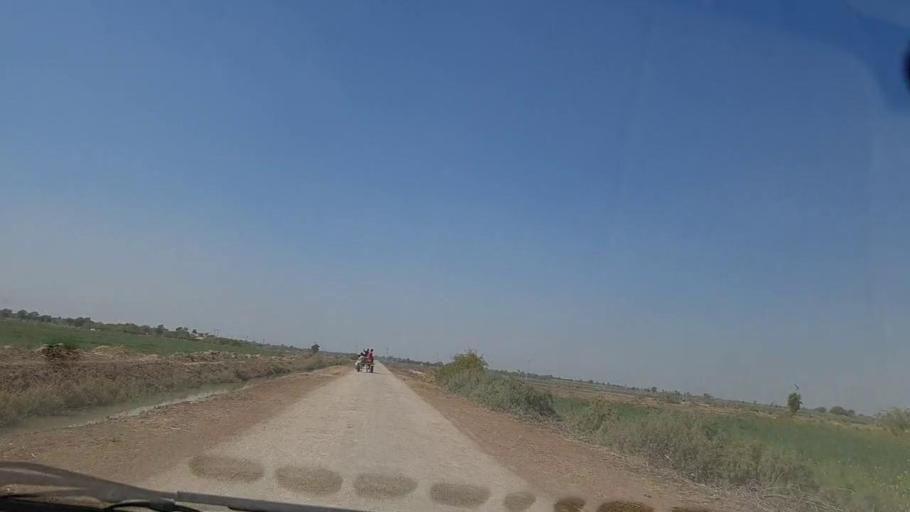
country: PK
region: Sindh
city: Mirwah Gorchani
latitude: 25.3702
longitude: 68.9892
